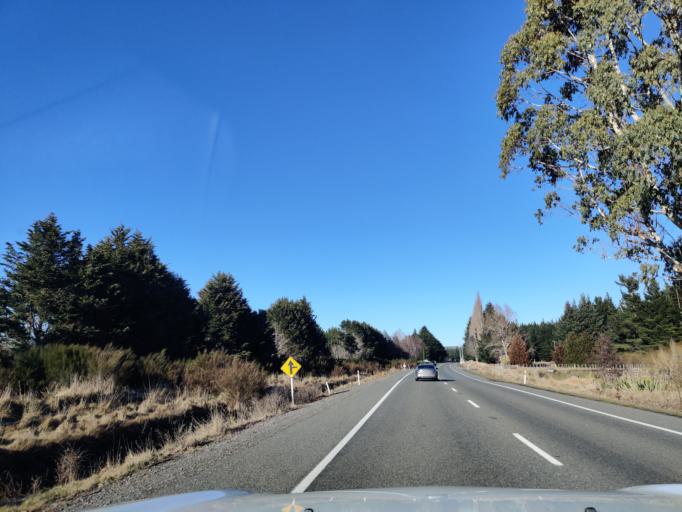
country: NZ
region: Manawatu-Wanganui
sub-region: Ruapehu District
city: Waiouru
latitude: -39.4649
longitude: 175.6731
